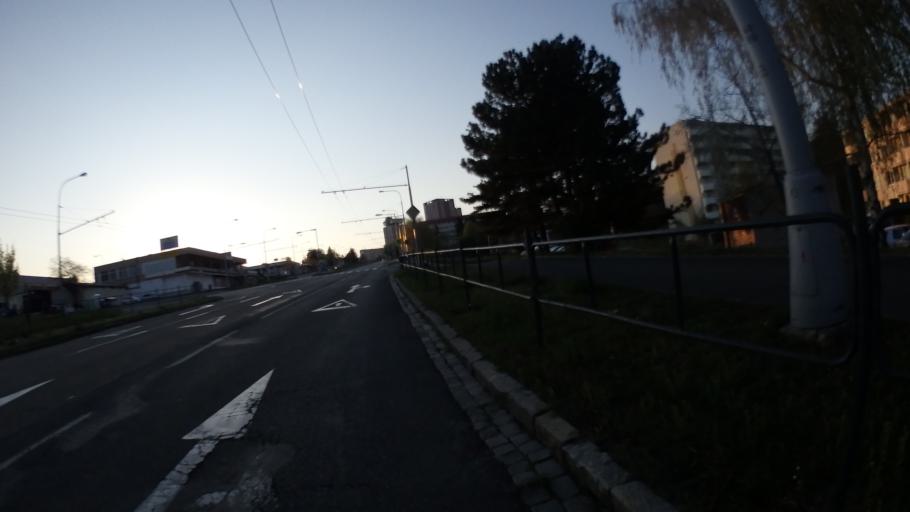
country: CZ
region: South Moravian
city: Ostopovice
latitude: 49.1941
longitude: 16.5414
